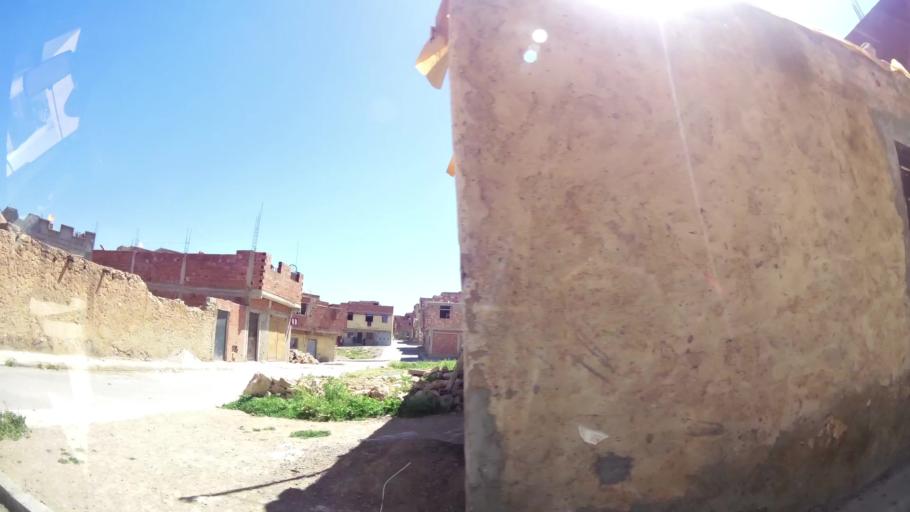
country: MA
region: Oriental
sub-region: Oujda-Angad
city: Oujda
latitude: 34.6494
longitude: -1.8750
